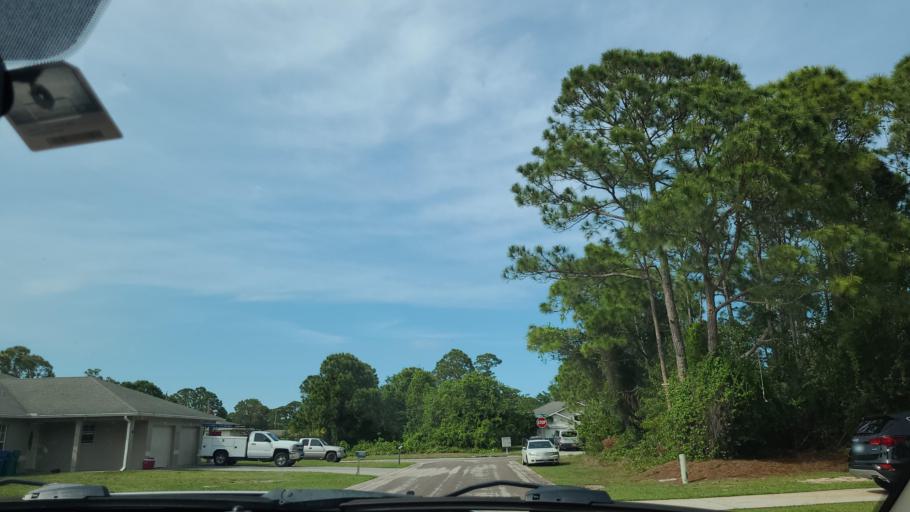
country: US
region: Florida
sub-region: Indian River County
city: Sebastian
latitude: 27.7722
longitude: -80.4640
